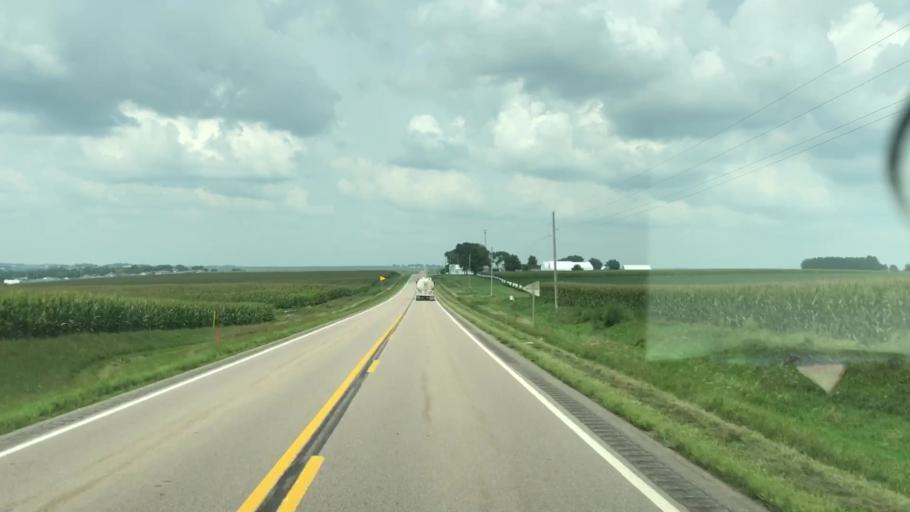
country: US
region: Iowa
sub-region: Plymouth County
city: Remsen
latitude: 42.7997
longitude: -95.9577
